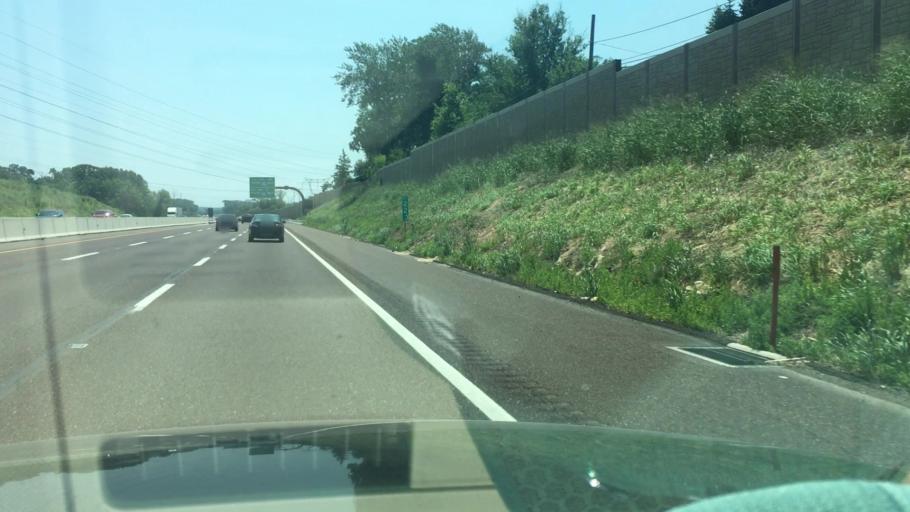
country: US
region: Pennsylvania
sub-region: Montgomery County
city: Blue Bell
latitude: 40.1450
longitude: -75.2907
